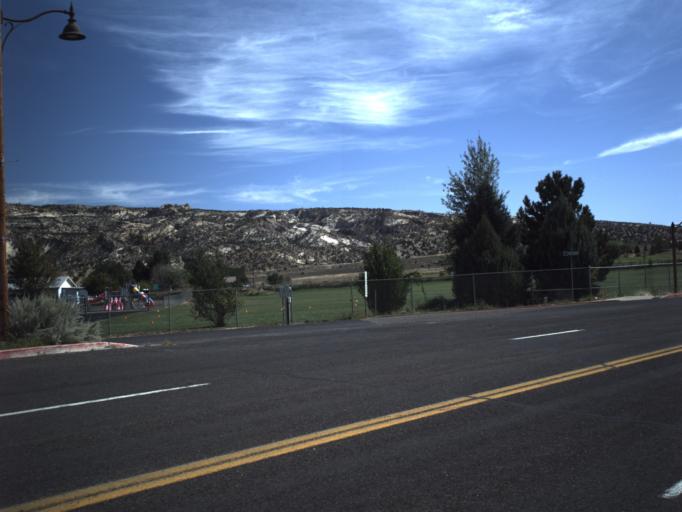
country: US
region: Utah
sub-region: Wayne County
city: Loa
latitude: 37.7697
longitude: -111.5949
